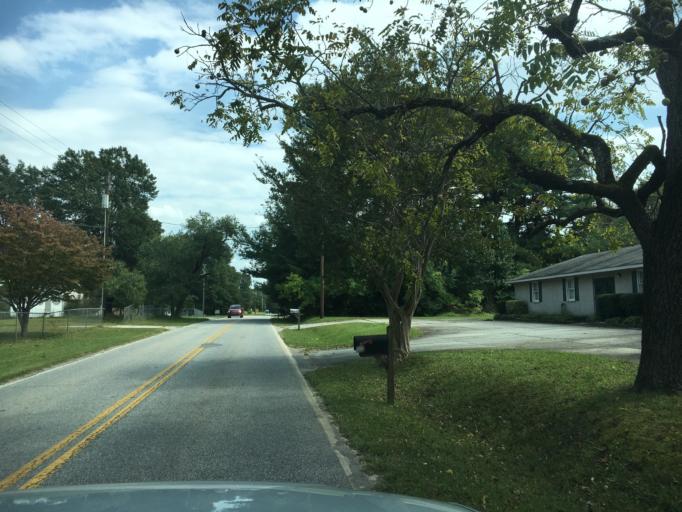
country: US
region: South Carolina
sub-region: Anderson County
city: Powdersville
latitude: 34.7868
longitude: -82.4762
